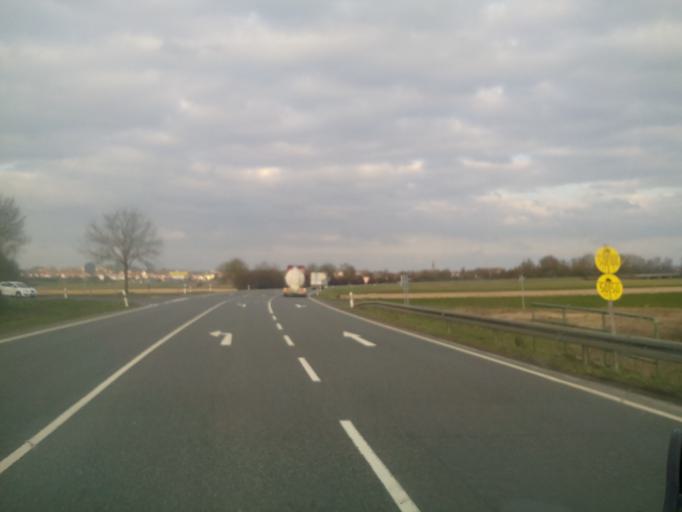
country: DE
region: Bavaria
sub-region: Regierungsbezirk Mittelfranken
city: Lonnerstadt
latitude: 49.7008
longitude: 10.7789
